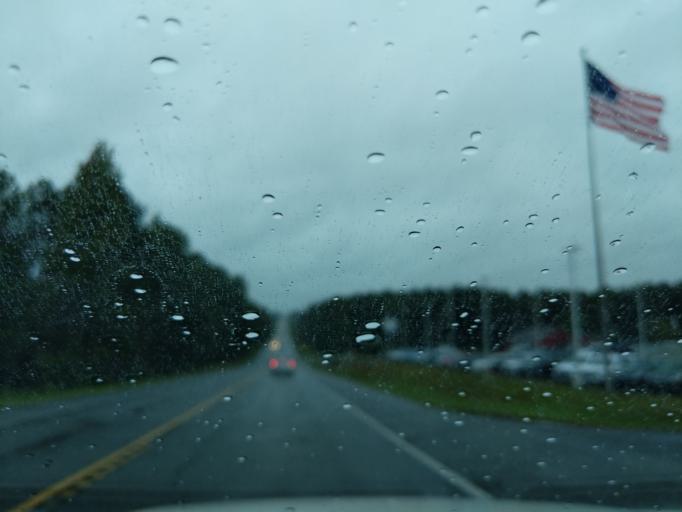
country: US
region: Louisiana
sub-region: Webster Parish
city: Minden
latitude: 32.6239
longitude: -93.2497
